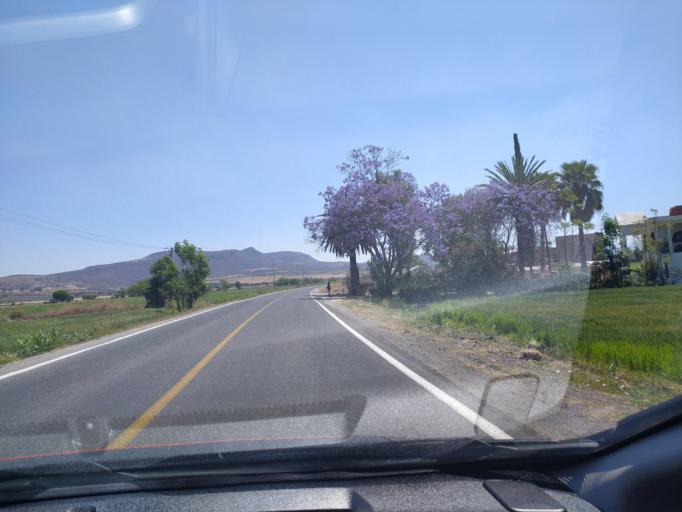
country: MX
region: Guanajuato
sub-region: San Francisco del Rincon
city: San Ignacio de Hidalgo
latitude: 20.8484
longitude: -101.8502
